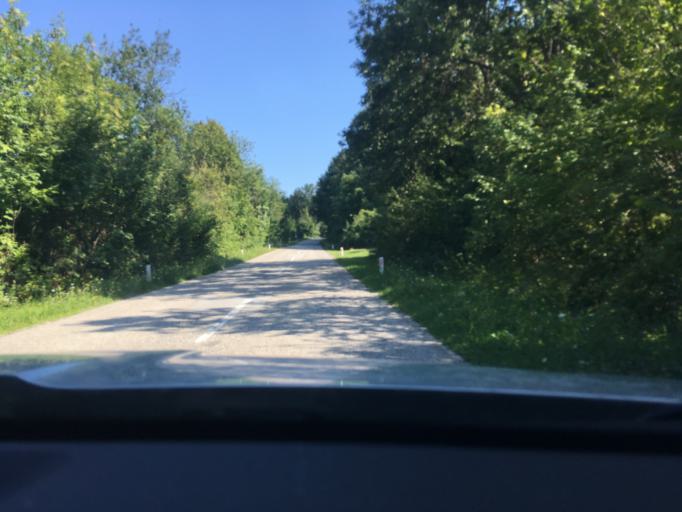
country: SI
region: Metlika
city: Metlika
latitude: 45.5039
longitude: 15.3401
